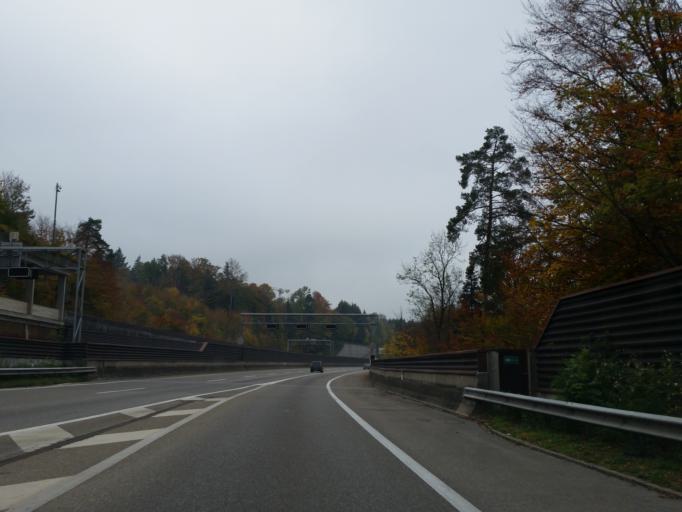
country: CH
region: Saint Gallen
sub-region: Wahlkreis St. Gallen
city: Sankt Gallen
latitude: 47.4275
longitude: 9.3585
